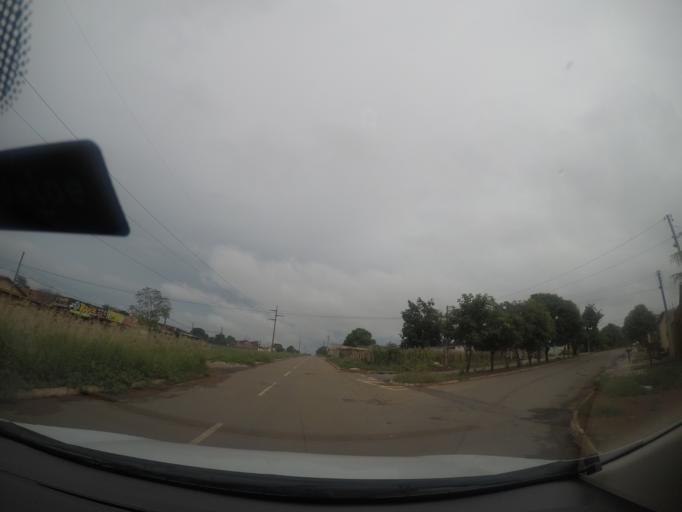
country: BR
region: Goias
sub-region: Aparecida De Goiania
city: Aparecida de Goiania
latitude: -16.7700
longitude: -49.2993
